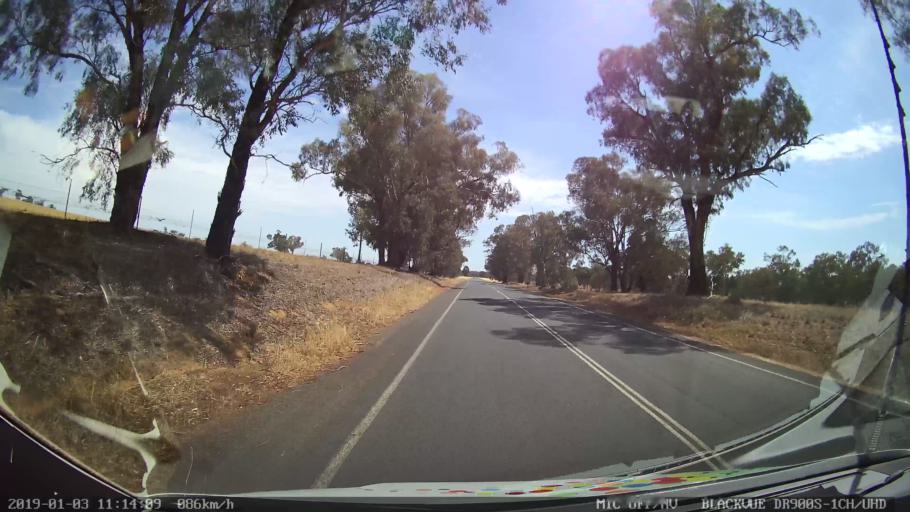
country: AU
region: New South Wales
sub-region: Young
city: Young
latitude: -34.1796
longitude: 148.2604
